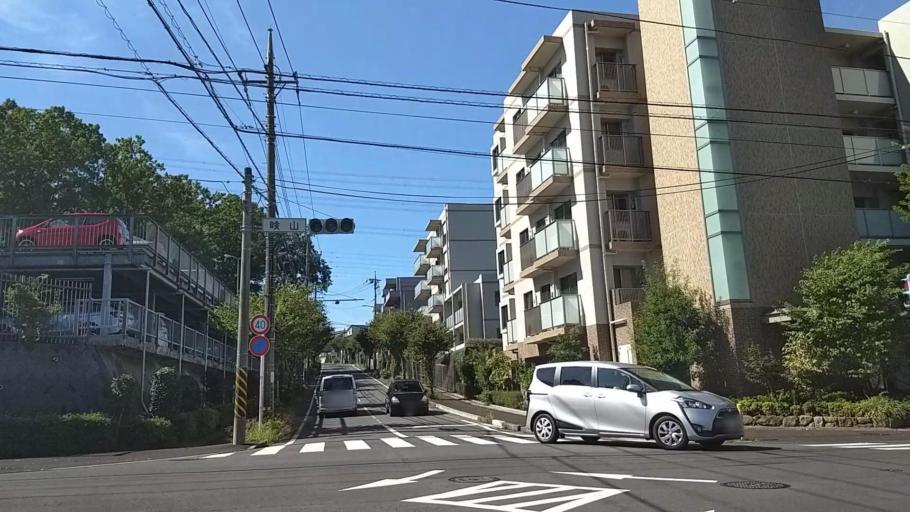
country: JP
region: Tokyo
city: Chofugaoka
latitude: 35.5719
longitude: 139.5388
